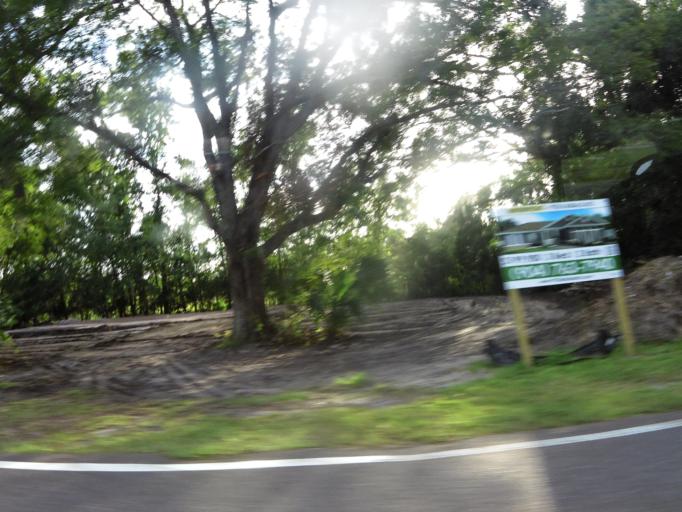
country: US
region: Florida
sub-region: Duval County
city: Jacksonville
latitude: 30.4135
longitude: -81.7321
